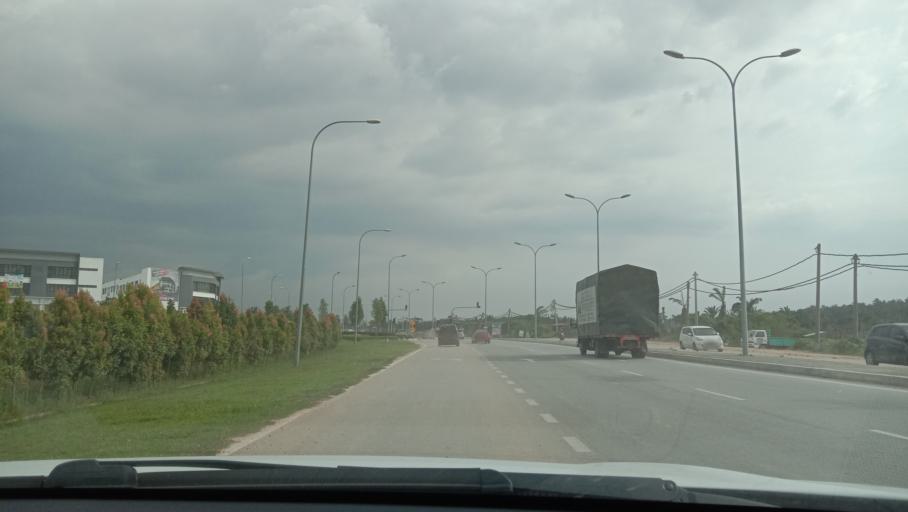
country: MY
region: Selangor
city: Ladang Seri Kundang
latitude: 3.2439
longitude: 101.4737
